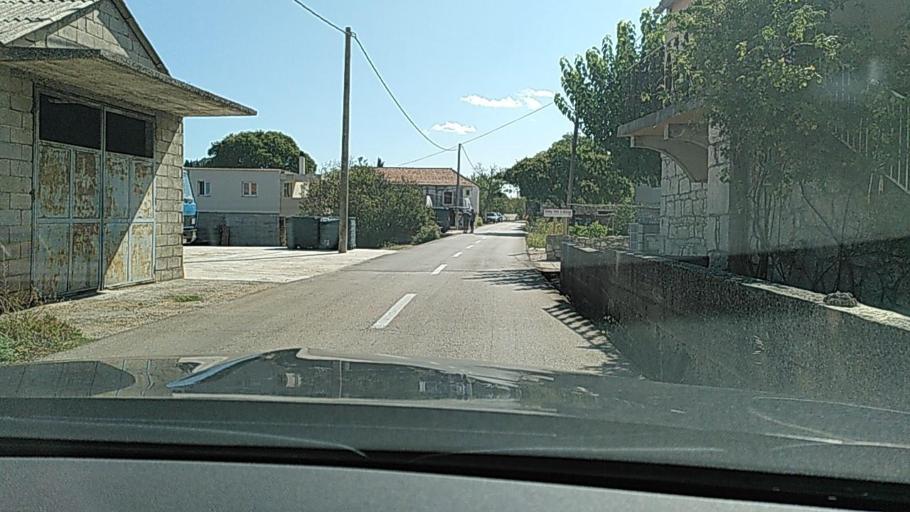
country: HR
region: Splitsko-Dalmatinska
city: Jelsa
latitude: 43.1461
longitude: 16.8324
